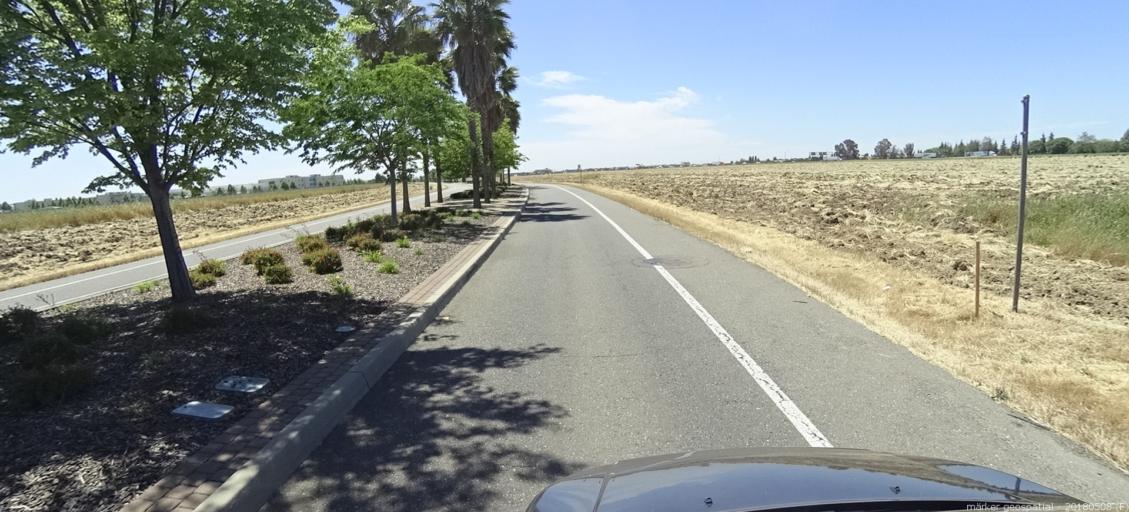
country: US
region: California
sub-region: Sacramento County
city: Elverta
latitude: 38.6703
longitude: -121.5361
